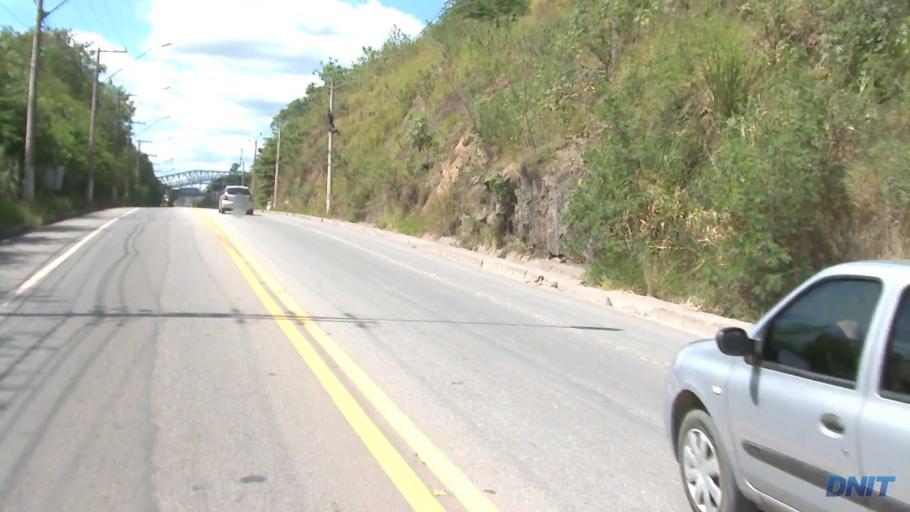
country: BR
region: Minas Gerais
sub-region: Coronel Fabriciano
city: Coronel Fabriciano
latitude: -19.5291
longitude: -42.6557
